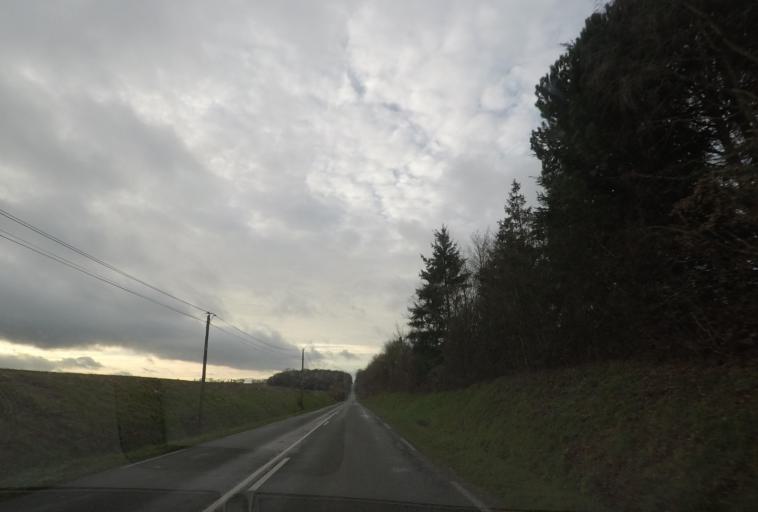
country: FR
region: Pays de la Loire
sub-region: Departement de la Sarthe
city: Saint-Calais
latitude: 47.9630
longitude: 0.7568
